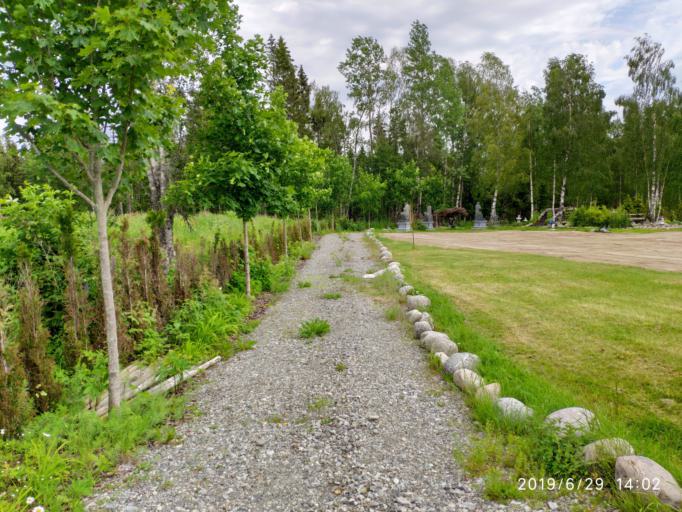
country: NO
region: Akershus
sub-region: Ullensaker
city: Jessheim
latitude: 60.1735
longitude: 11.1696
